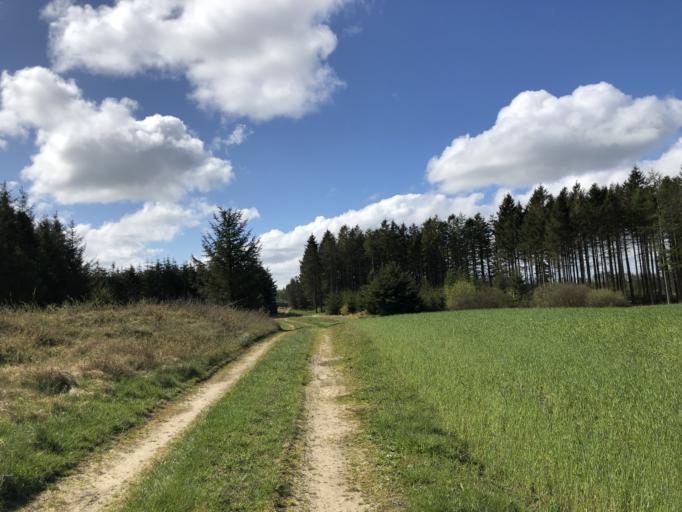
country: DK
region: Central Jutland
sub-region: Holstebro Kommune
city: Ulfborg
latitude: 56.2430
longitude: 8.4686
